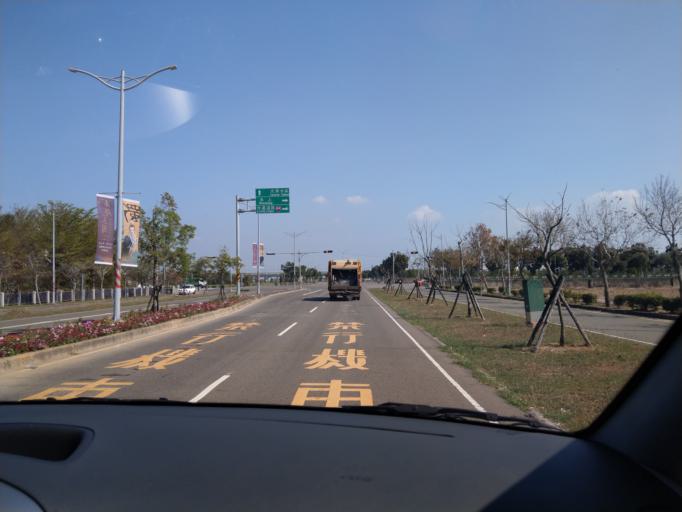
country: TW
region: Taiwan
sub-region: Chiayi
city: Taibao
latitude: 23.4662
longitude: 120.3171
